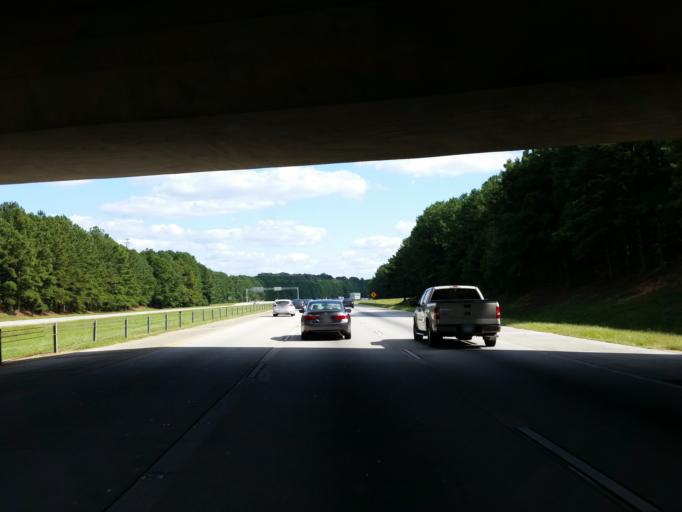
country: US
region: Georgia
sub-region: Clayton County
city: Conley
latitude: 33.6332
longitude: -84.3041
